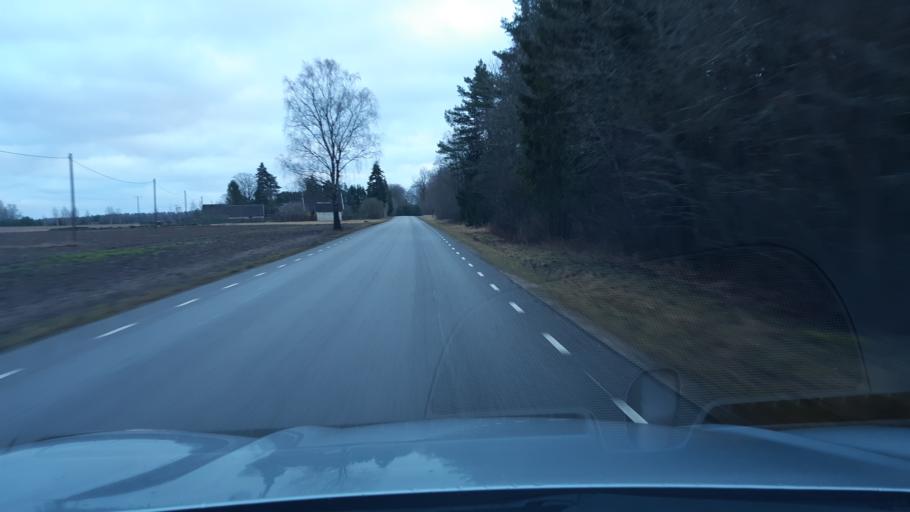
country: EE
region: Harju
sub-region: Saue linn
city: Saue
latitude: 59.2327
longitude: 24.5070
